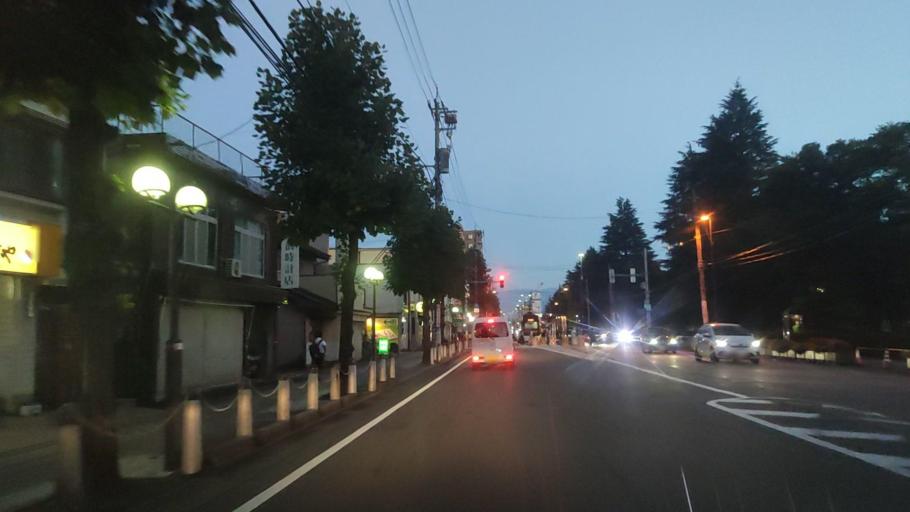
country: JP
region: Toyama
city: Toyama-shi
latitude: 36.6993
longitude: 137.1905
